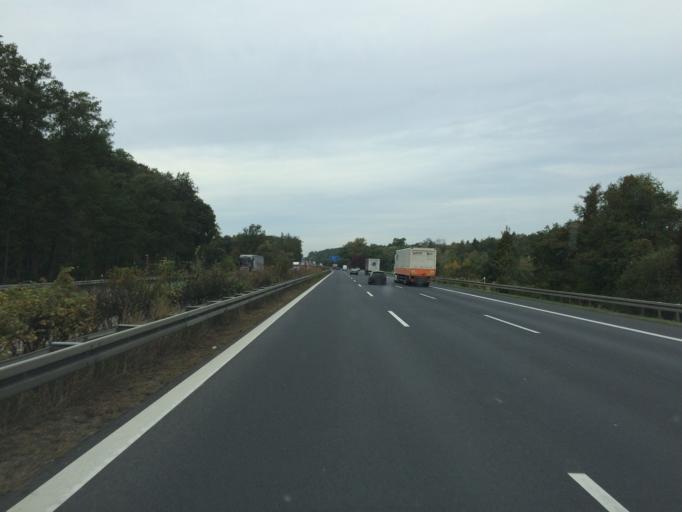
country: DE
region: Brandenburg
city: Michendorf
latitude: 52.3020
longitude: 13.1311
